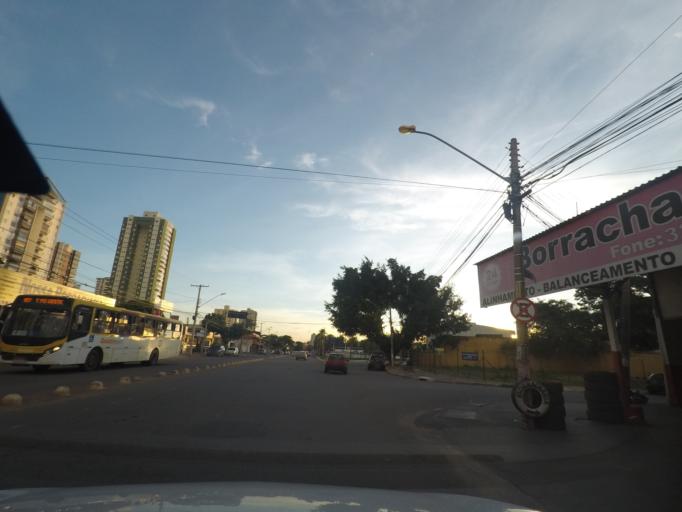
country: BR
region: Goias
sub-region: Goiania
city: Goiania
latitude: -16.6868
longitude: -49.2791
